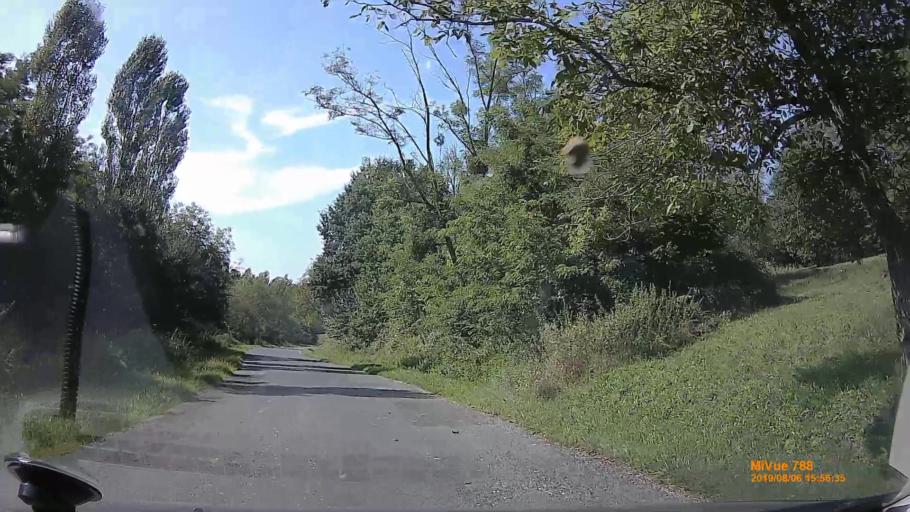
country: HU
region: Somogy
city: Csurgo
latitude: 46.2913
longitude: 17.0103
